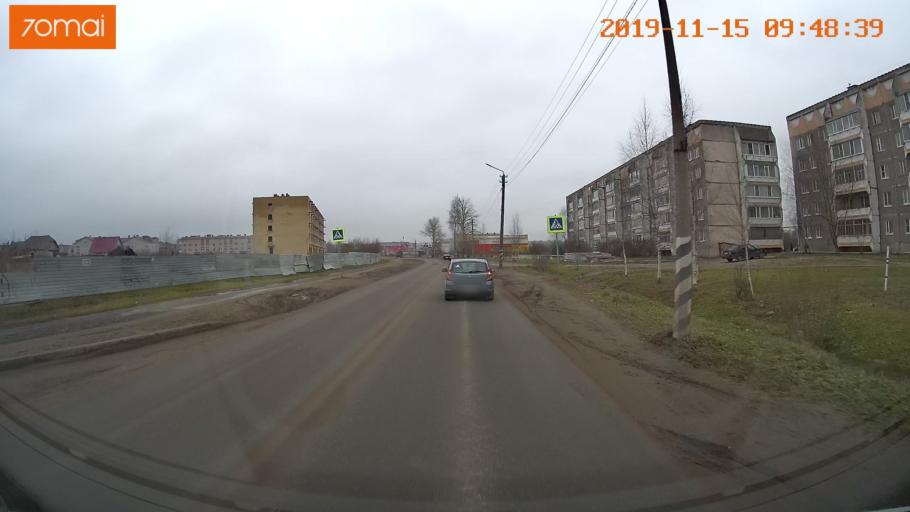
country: RU
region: Vologda
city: Sheksna
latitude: 59.2244
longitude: 38.5133
